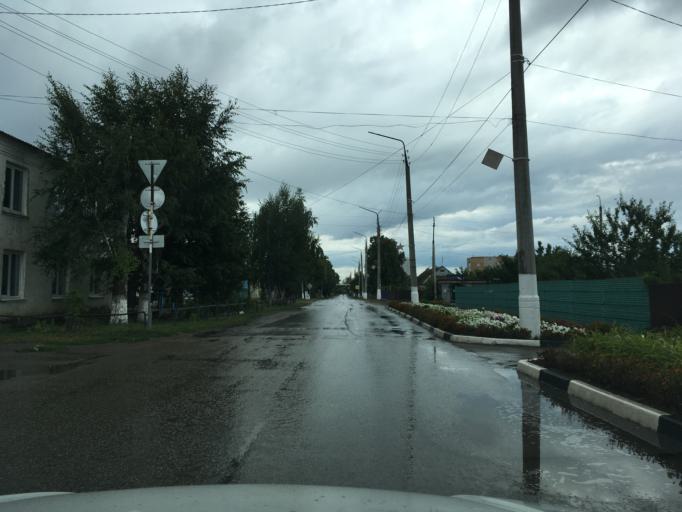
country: RU
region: Samara
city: Bezenchuk
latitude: 52.9833
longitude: 49.4395
